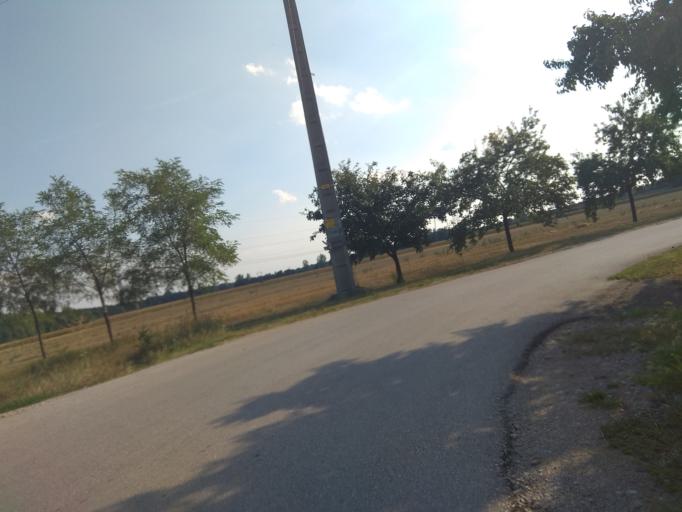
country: HU
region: Borsod-Abauj-Zemplen
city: Mezokeresztes
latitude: 47.8786
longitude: 20.6852
